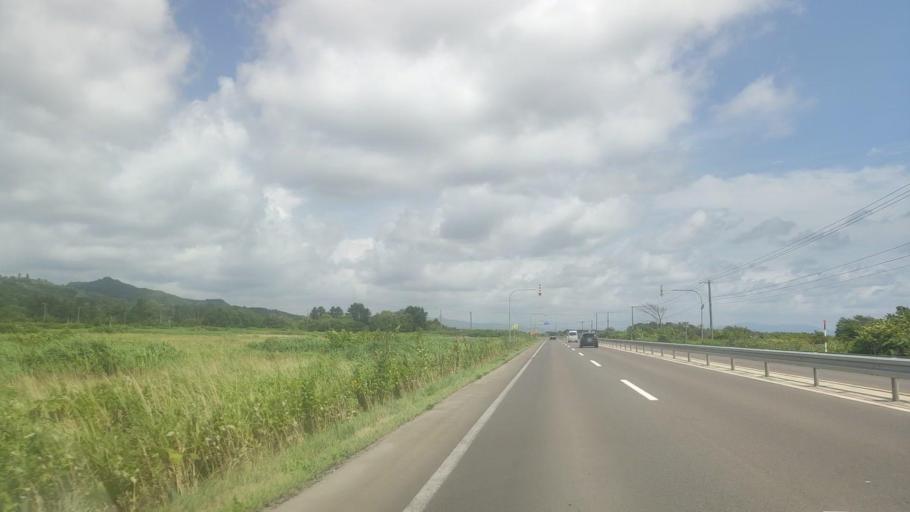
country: JP
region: Hokkaido
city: Niseko Town
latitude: 42.4467
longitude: 140.3291
